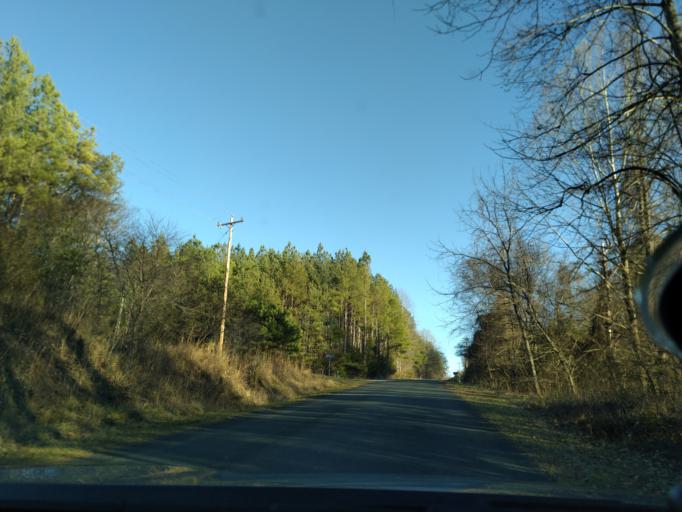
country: US
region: Virginia
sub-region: Buckingham County
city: Buckingham
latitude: 37.3729
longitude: -78.6305
